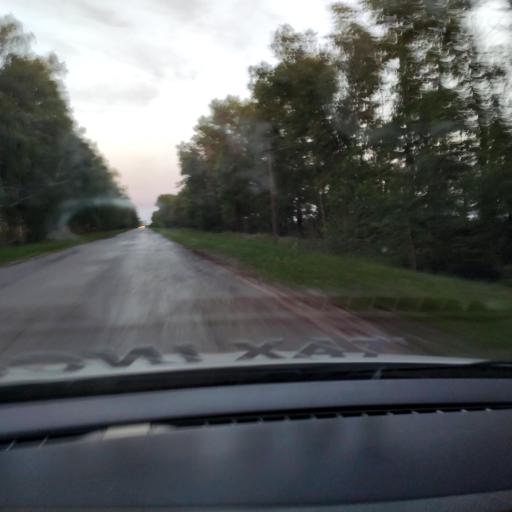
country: RU
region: Voronezj
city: Maslovka
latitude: 51.4394
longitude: 39.2876
